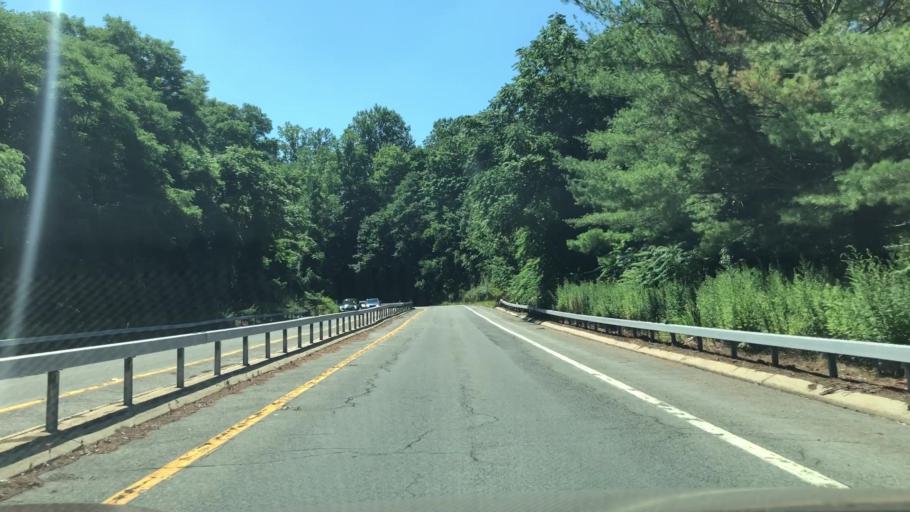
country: US
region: New York
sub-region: Westchester County
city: Harrison
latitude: 40.9840
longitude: -73.7451
